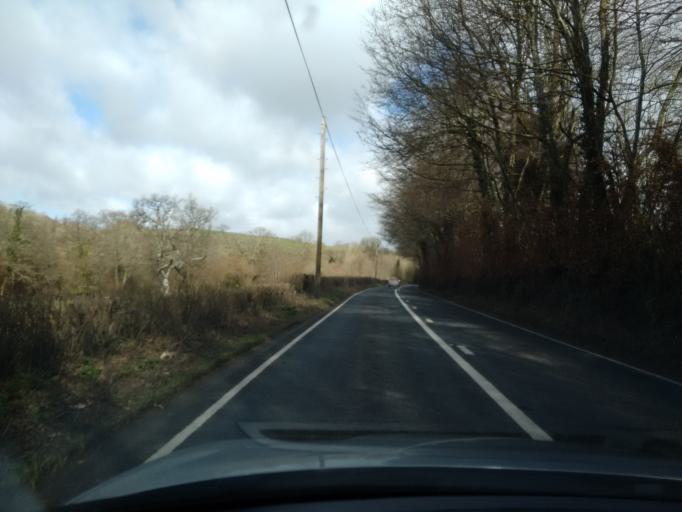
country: GB
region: England
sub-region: Cornwall
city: Launceston
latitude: 50.5995
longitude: -4.3377
